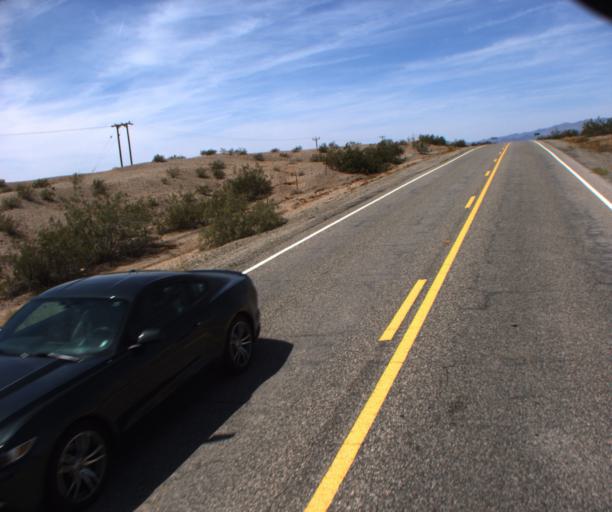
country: US
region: Arizona
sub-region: La Paz County
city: Parker
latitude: 34.0210
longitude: -114.2505
